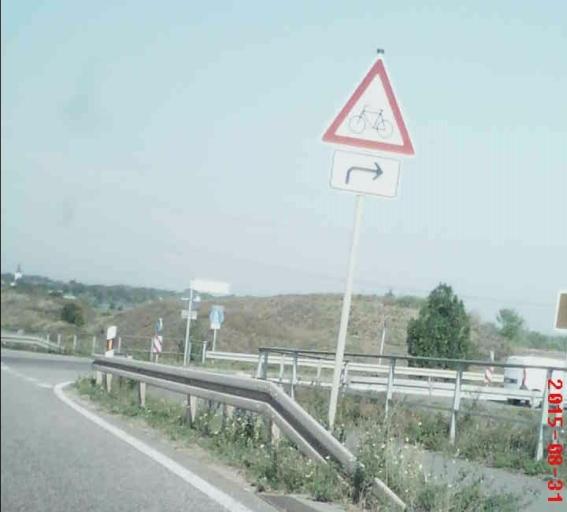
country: DE
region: Thuringia
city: Kleinmolsen
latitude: 51.0420
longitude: 11.0650
